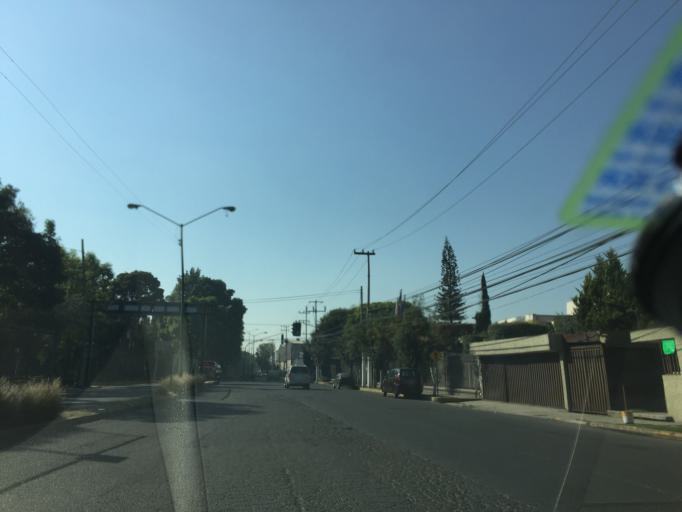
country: MX
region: Mexico
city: Vista Hermosa
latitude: 19.5075
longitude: -99.2114
